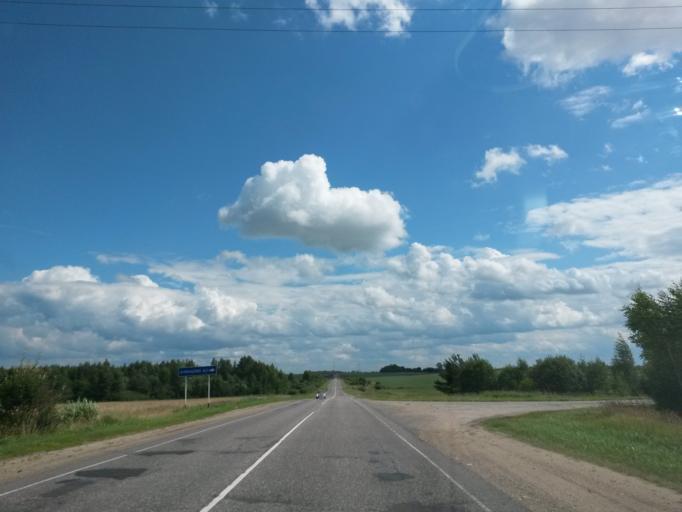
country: RU
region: Ivanovo
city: Pistsovo
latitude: 57.1853
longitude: 40.4616
